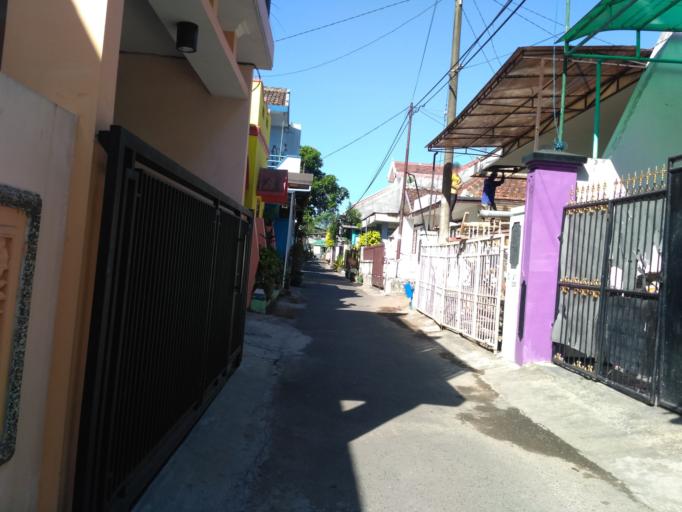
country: ID
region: East Java
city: Singosari
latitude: -7.9276
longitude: 112.6519
